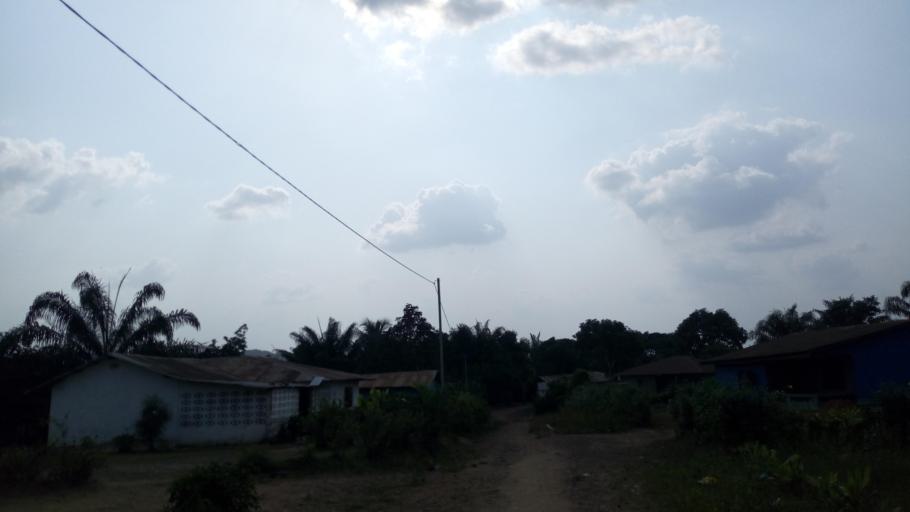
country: SL
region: Southern Province
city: Mogbwemo
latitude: 7.7627
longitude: -12.3146
